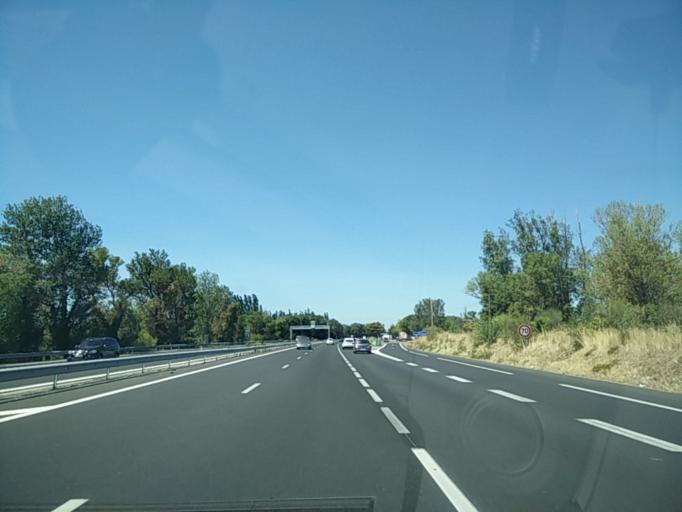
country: FR
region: Provence-Alpes-Cote d'Azur
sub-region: Departement du Vaucluse
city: Cavaillon
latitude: 43.8308
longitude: 5.0128
